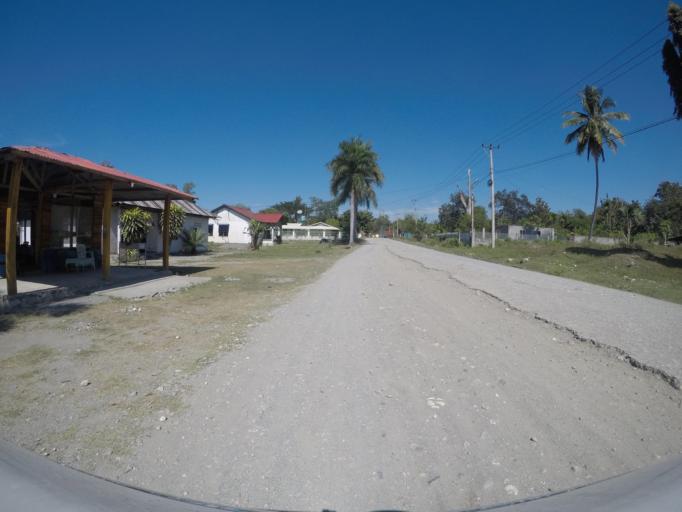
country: TL
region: Viqueque
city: Viqueque
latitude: -8.9766
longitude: 126.0445
